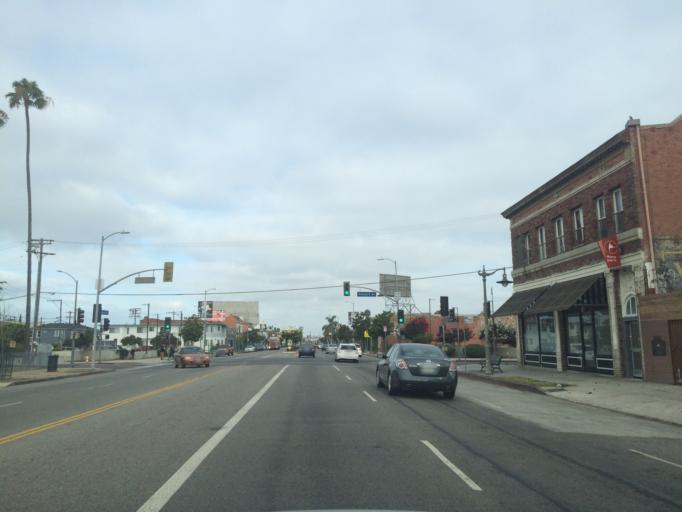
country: US
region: California
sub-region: Los Angeles County
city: View Park-Windsor Hills
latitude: 34.0399
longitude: -118.3391
